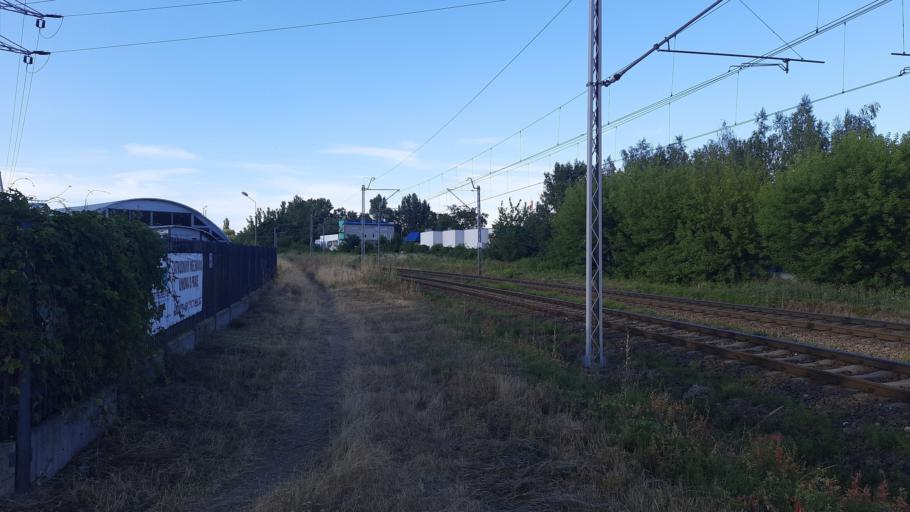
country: PL
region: Lodz Voivodeship
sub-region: Powiat lodzki wschodni
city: Starowa Gora
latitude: 51.7279
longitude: 19.5078
